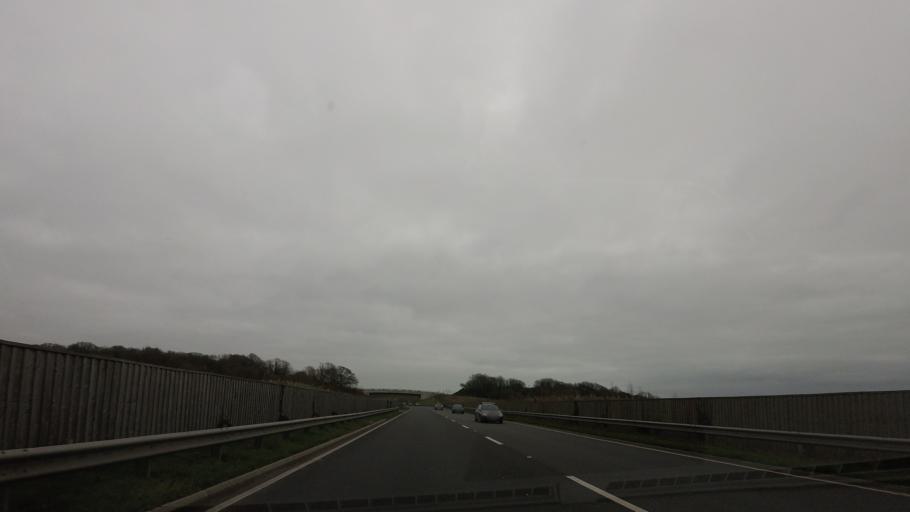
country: GB
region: England
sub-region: East Sussex
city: Bexhill-on-Sea
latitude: 50.8684
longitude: 0.5004
